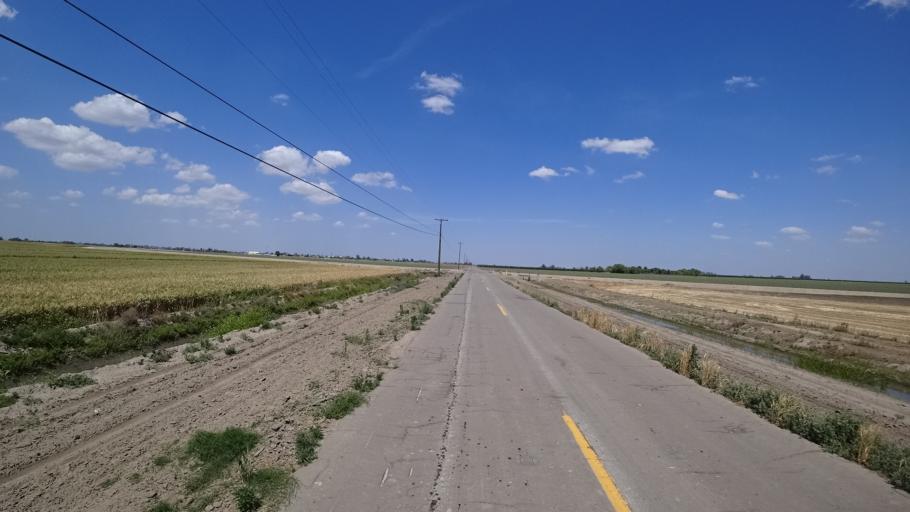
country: US
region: California
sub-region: Kings County
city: Stratford
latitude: 36.1713
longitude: -119.8161
